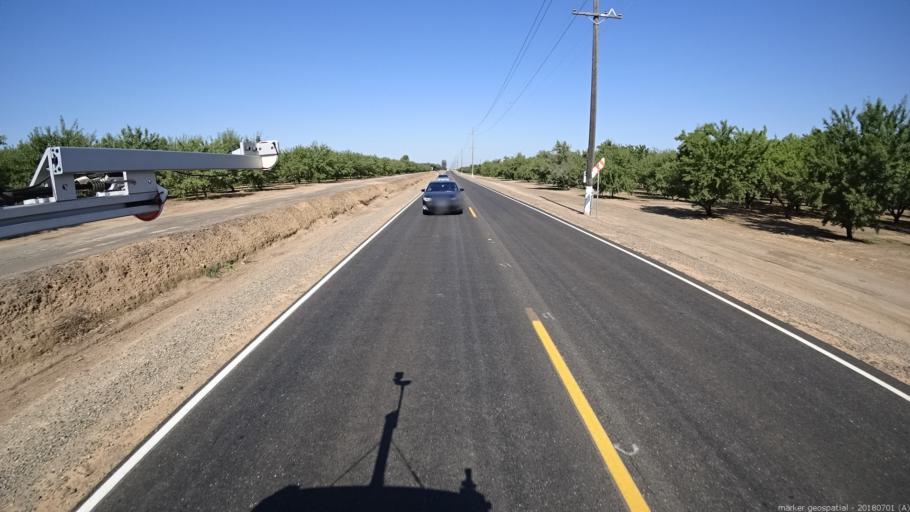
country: US
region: California
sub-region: Madera County
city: Bonadelle Ranchos-Madera Ranchos
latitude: 36.8804
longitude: -119.8856
